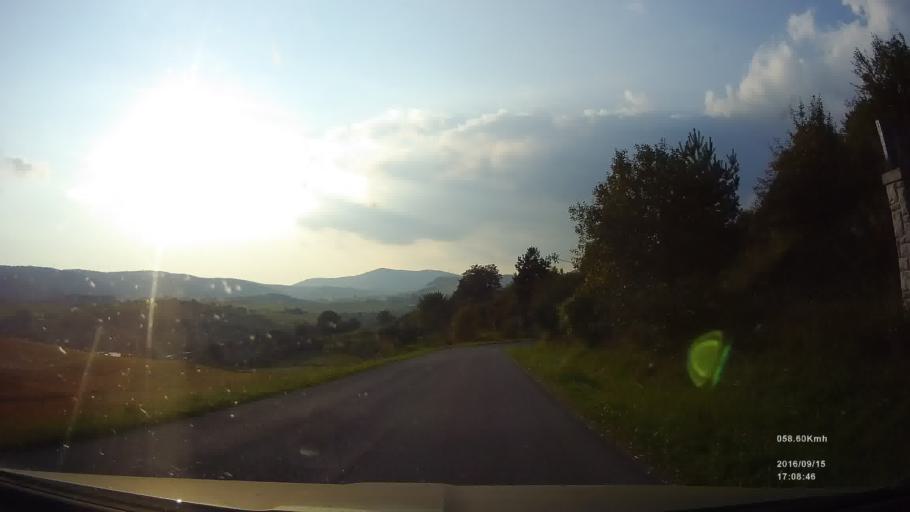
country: SK
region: Presovsky
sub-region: Okres Presov
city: Presov
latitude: 48.9153
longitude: 21.1309
